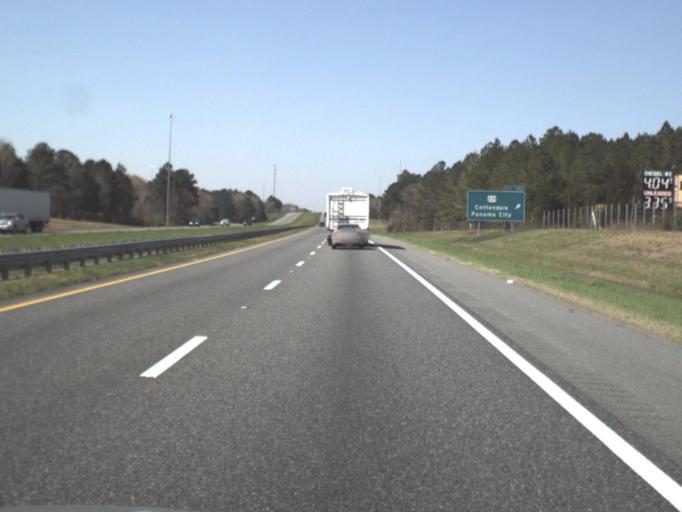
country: US
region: Florida
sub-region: Jackson County
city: Marianna
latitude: 30.7548
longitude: -85.3716
